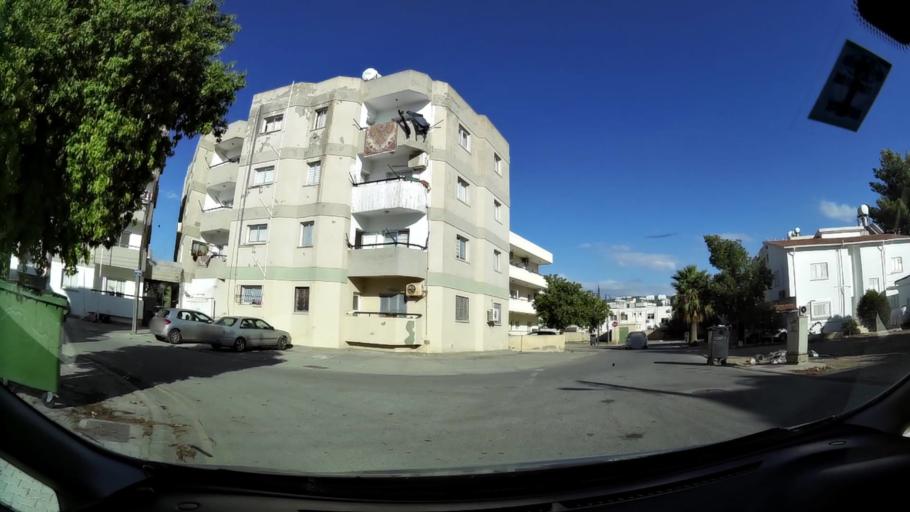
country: CY
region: Lefkosia
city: Nicosia
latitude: 35.1977
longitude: 33.3416
